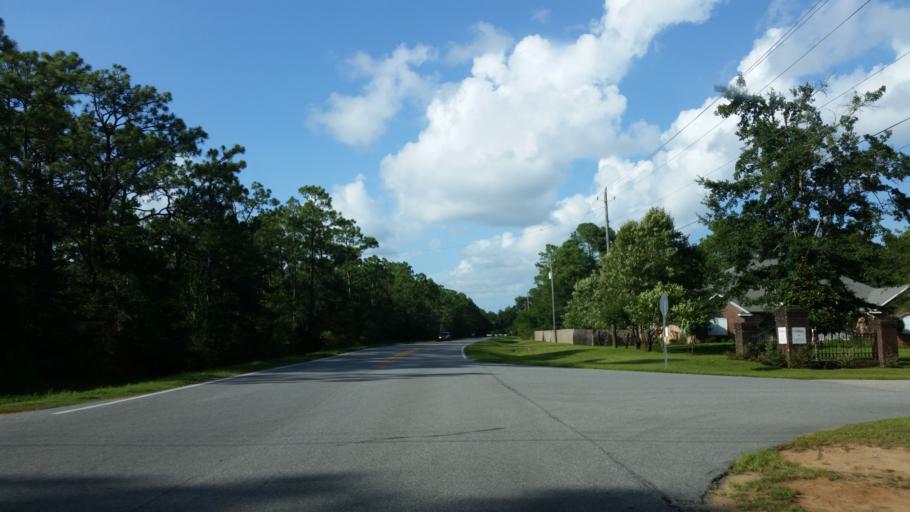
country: US
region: Florida
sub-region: Santa Rosa County
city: Bagdad
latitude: 30.4974
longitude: -87.0625
